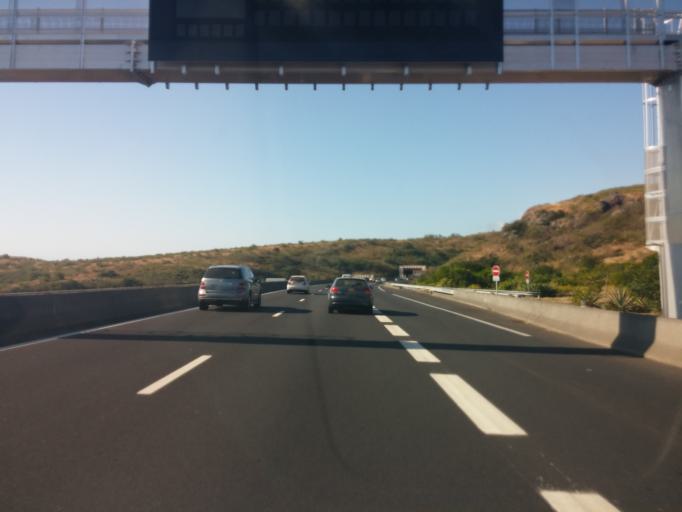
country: RE
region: Reunion
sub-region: Reunion
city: Saint-Paul
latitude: -21.0340
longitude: 55.2502
